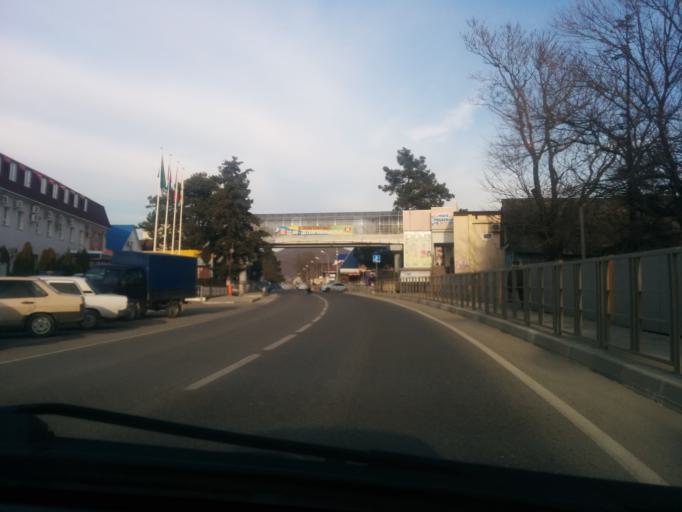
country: RU
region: Krasnodarskiy
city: Novomikhaylovskiy
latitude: 44.2532
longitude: 38.8454
